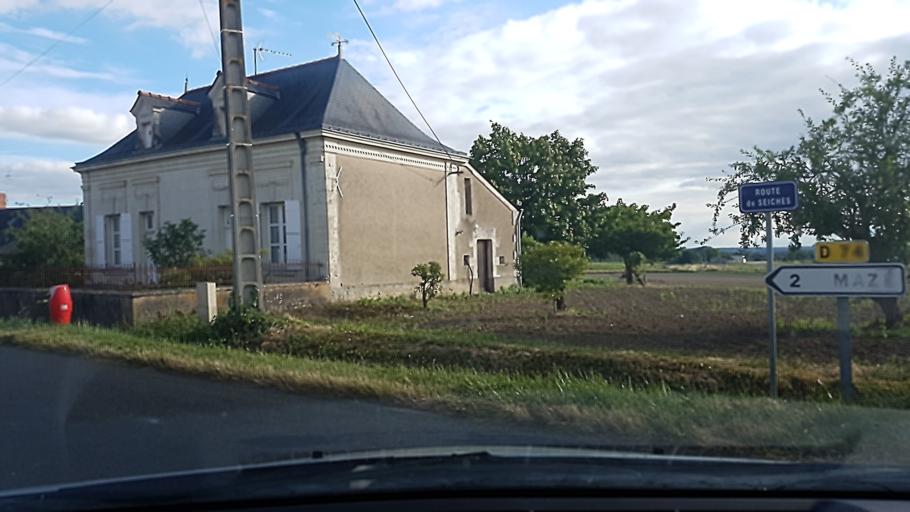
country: FR
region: Pays de la Loire
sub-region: Departement de Maine-et-Loire
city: Maze
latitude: 47.4706
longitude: -0.2830
